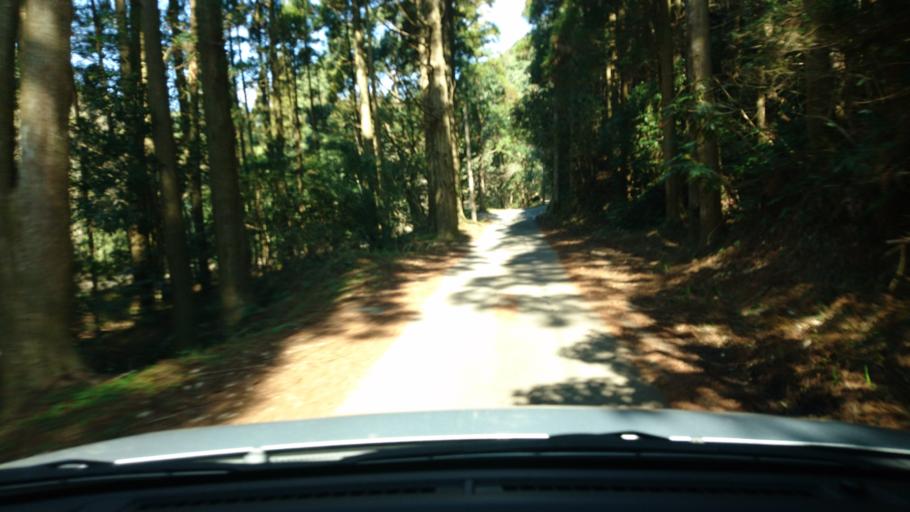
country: JP
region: Miyazaki
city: Miyazaki-shi
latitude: 31.8264
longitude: 131.3965
